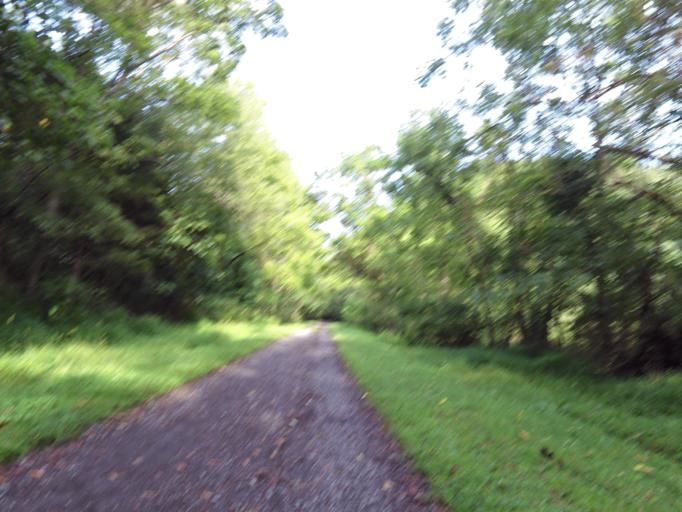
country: US
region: Virginia
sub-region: Washington County
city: Abingdon
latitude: 36.6973
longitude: -81.9474
